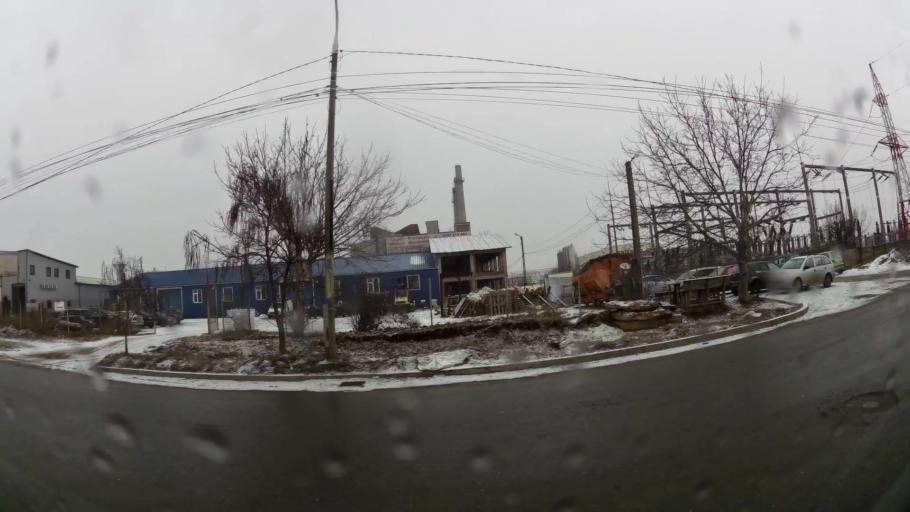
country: RO
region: Dambovita
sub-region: Municipiul Targoviste
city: Targoviste
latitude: 44.9251
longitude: 25.4326
